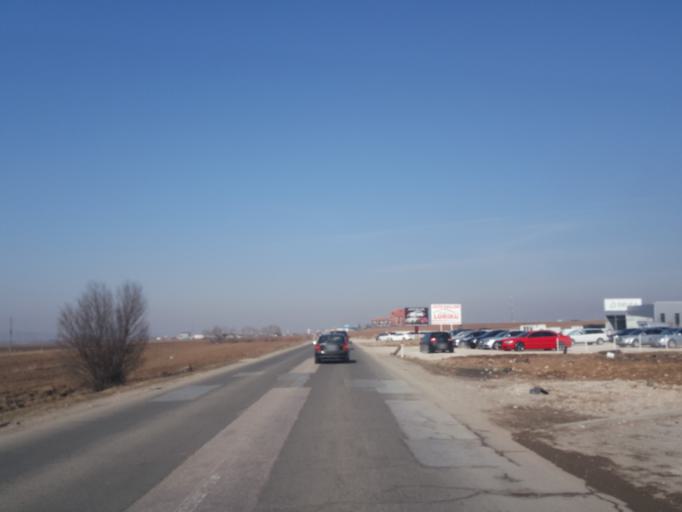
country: XK
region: Mitrovica
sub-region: Vushtrri
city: Vushtrri
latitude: 42.7697
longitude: 21.0216
